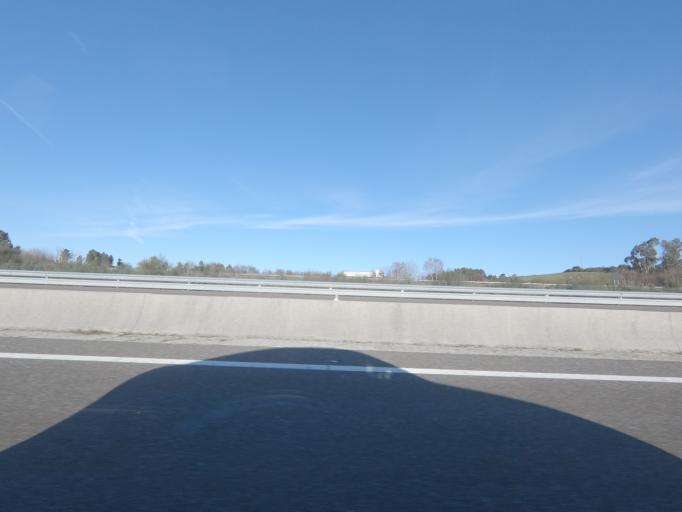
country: ES
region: Galicia
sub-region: Provincia de Pontevedra
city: Dozon
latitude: 42.5763
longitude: -8.0620
